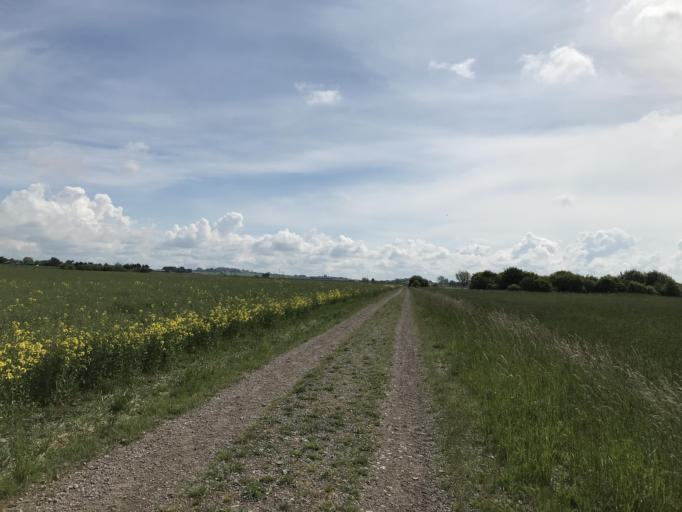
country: SE
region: Skane
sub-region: Landskrona
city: Landskrona
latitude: 55.8996
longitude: 12.8401
